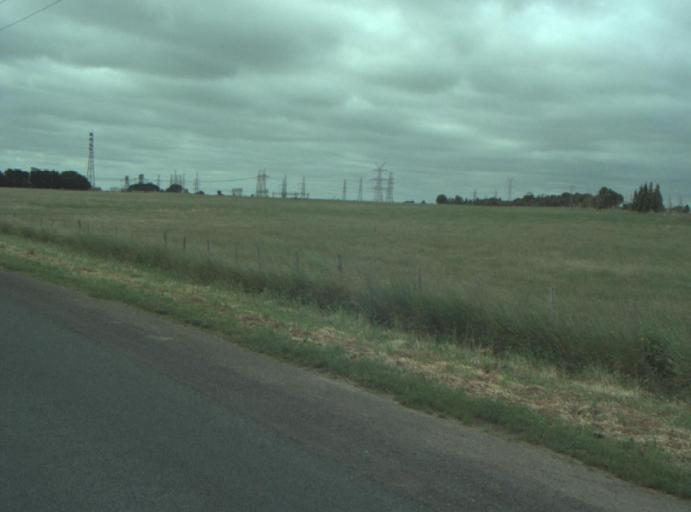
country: AU
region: Victoria
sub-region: Greater Geelong
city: Bell Post Hill
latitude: -38.0267
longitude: 144.2902
